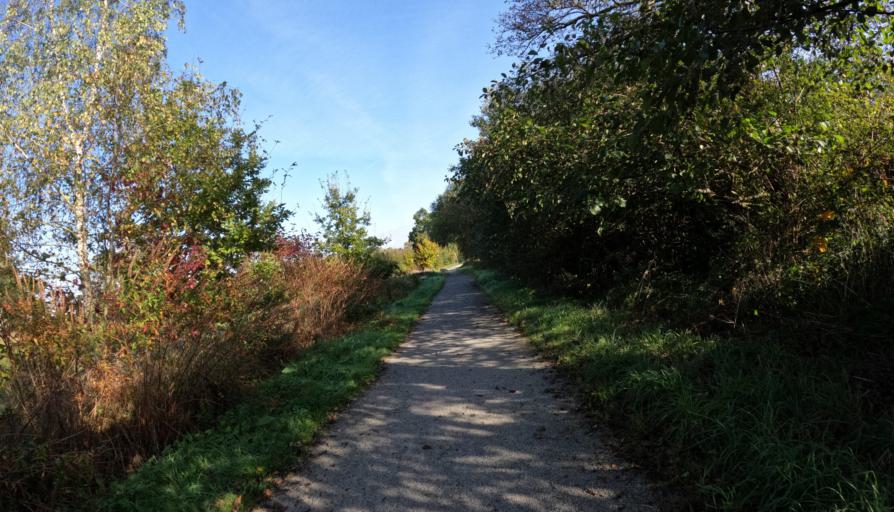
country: FR
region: Brittany
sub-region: Departement d'Ille-et-Vilaine
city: Betton
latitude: 48.1730
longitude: -1.6600
